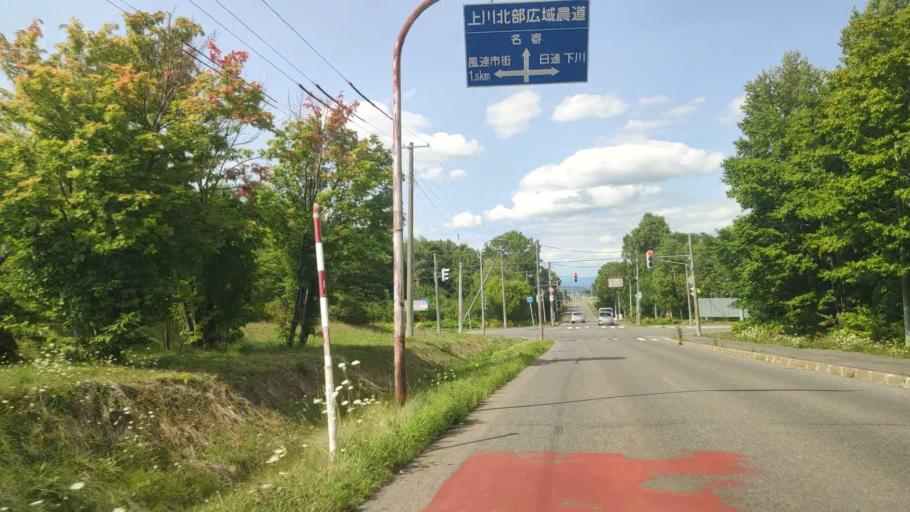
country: JP
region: Hokkaido
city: Nayoro
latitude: 44.2856
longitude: 142.4295
